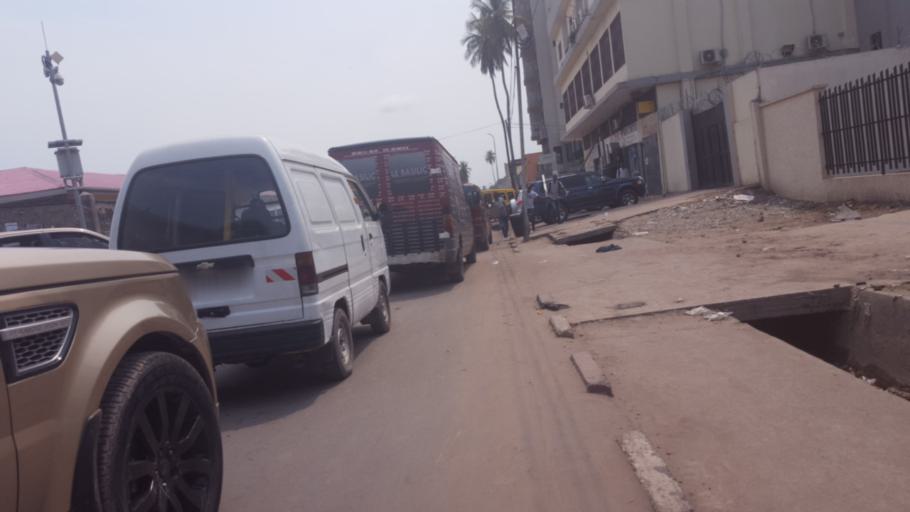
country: CD
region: Kinshasa
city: Kinshasa
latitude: -4.3065
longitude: 15.3064
